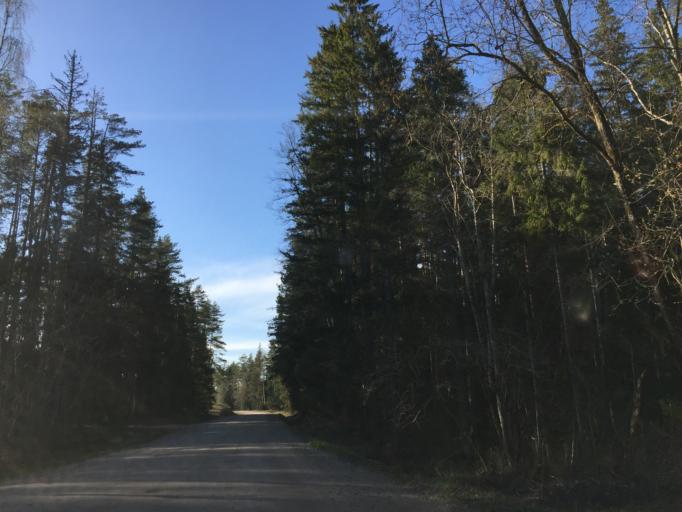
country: LV
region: Valkas Rajons
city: Valka
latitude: 57.7969
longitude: 25.9632
